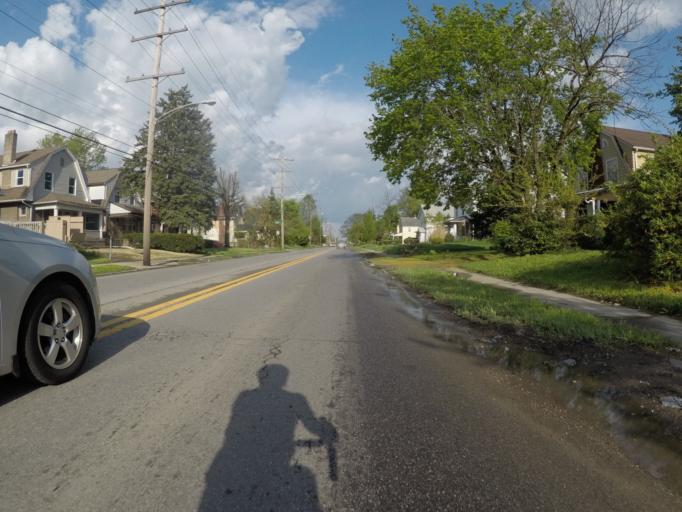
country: US
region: Ohio
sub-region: Franklin County
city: Bexley
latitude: 40.0138
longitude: -82.9708
